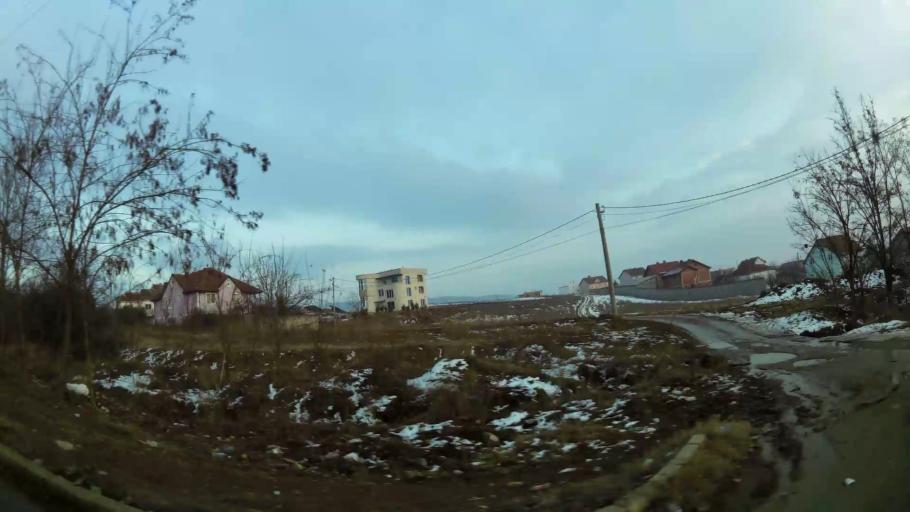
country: MK
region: Aracinovo
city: Arachinovo
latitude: 42.0246
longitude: 21.5722
